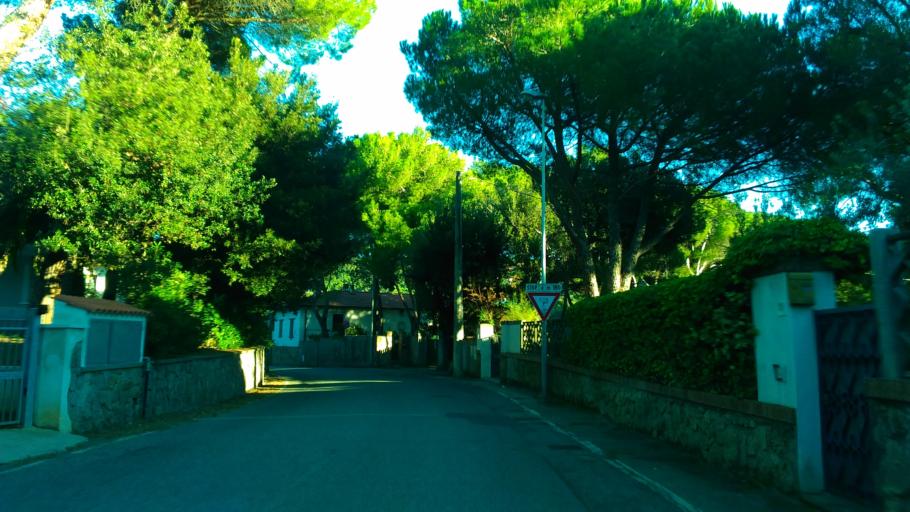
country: IT
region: Tuscany
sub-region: Provincia di Livorno
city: Quercianella
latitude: 43.4499
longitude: 10.3771
